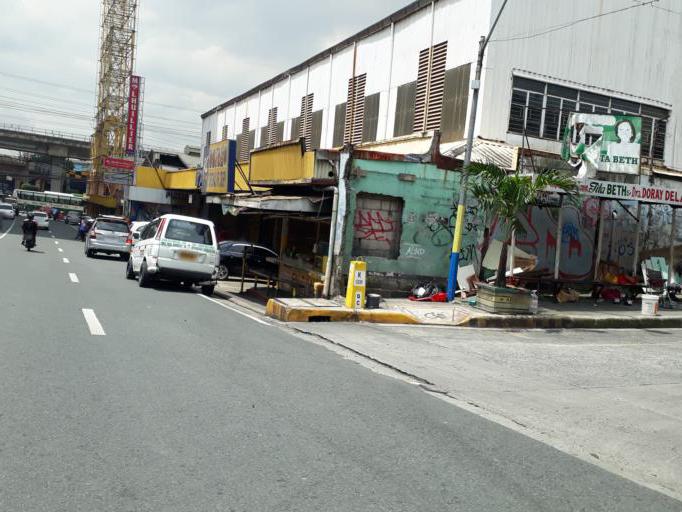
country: PH
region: Calabarzon
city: Bagong Pagasa
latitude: 14.6583
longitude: 121.0243
